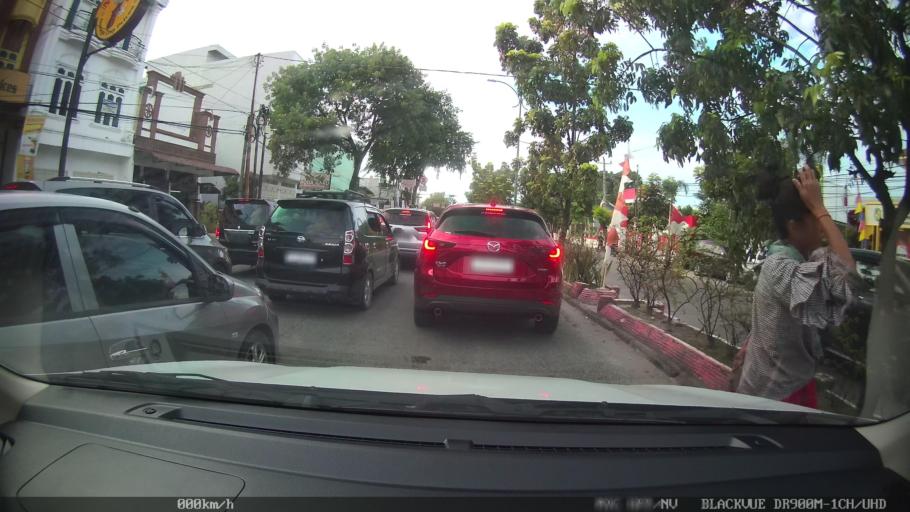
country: ID
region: North Sumatra
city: Medan
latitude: 3.6221
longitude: 98.6809
